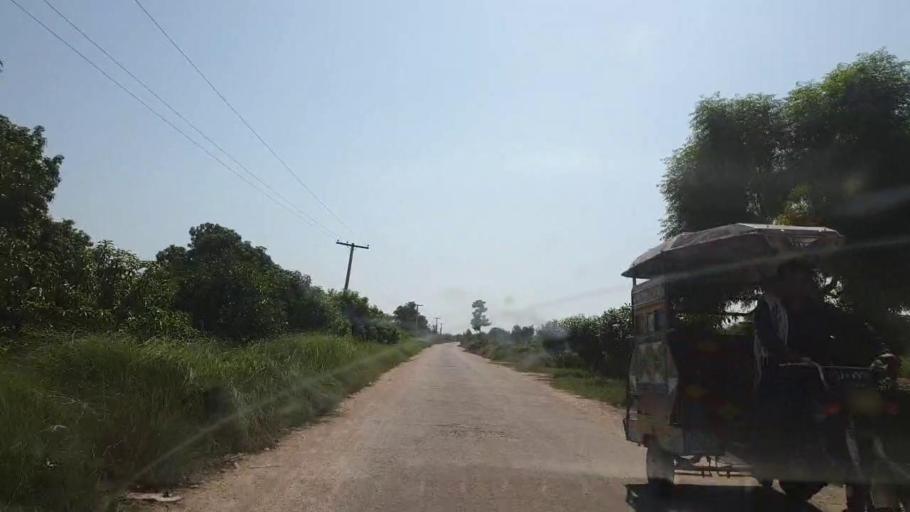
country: PK
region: Sindh
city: Tando Jam
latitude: 25.4367
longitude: 68.5840
